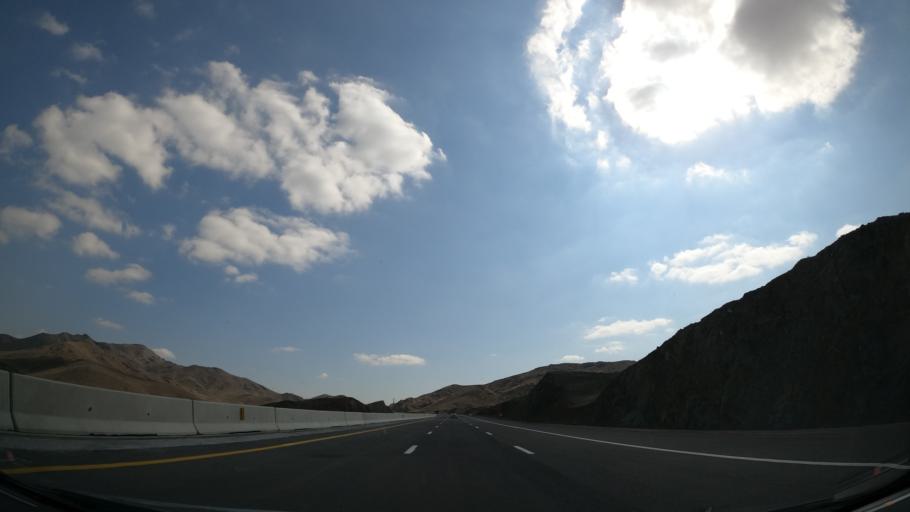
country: IR
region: Alborz
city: Nazarabad
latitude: 35.6894
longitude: 50.6354
